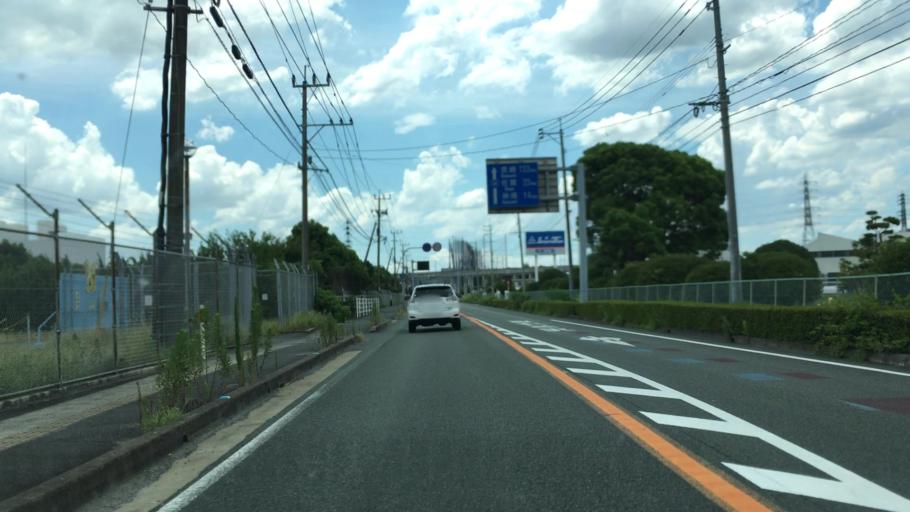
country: JP
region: Saga Prefecture
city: Tosu
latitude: 33.3642
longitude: 130.5009
